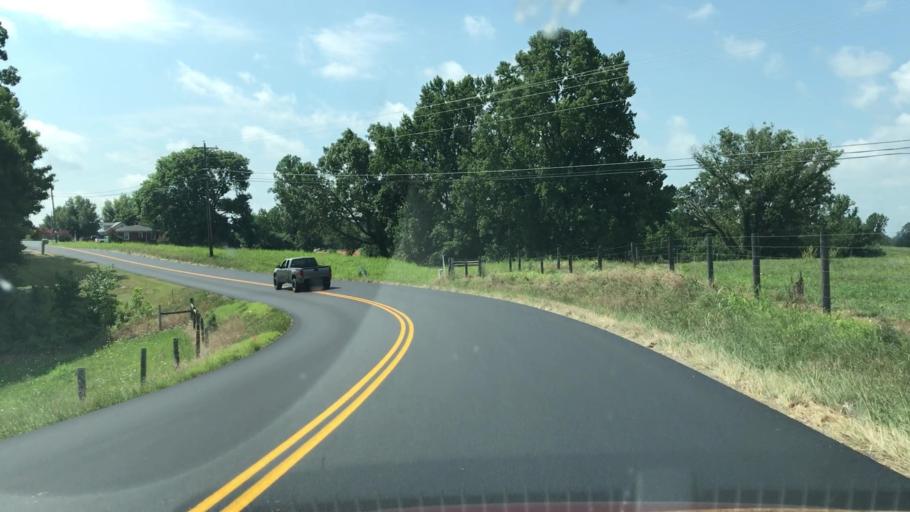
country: US
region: Kentucky
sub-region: Monroe County
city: Tompkinsville
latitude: 36.7236
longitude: -85.7210
